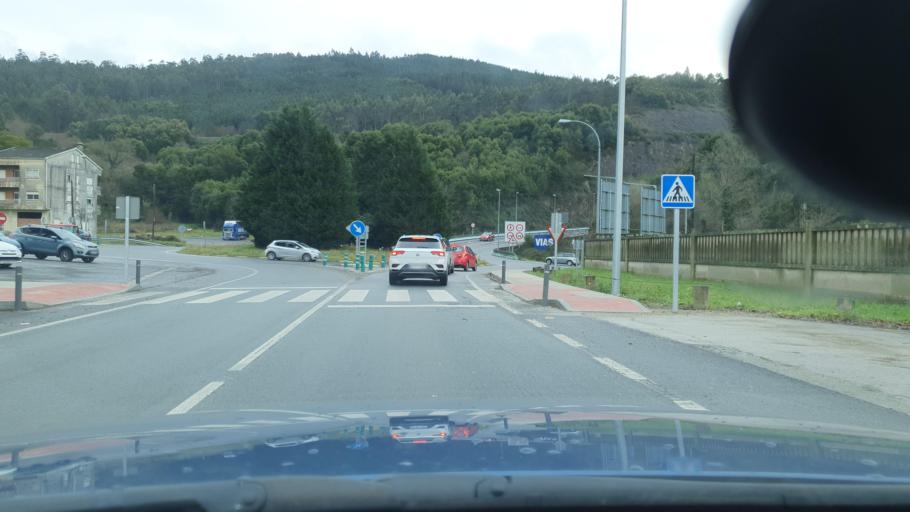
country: ES
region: Galicia
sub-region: Provincia da Coruna
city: Padron
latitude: 42.7561
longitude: -8.6527
